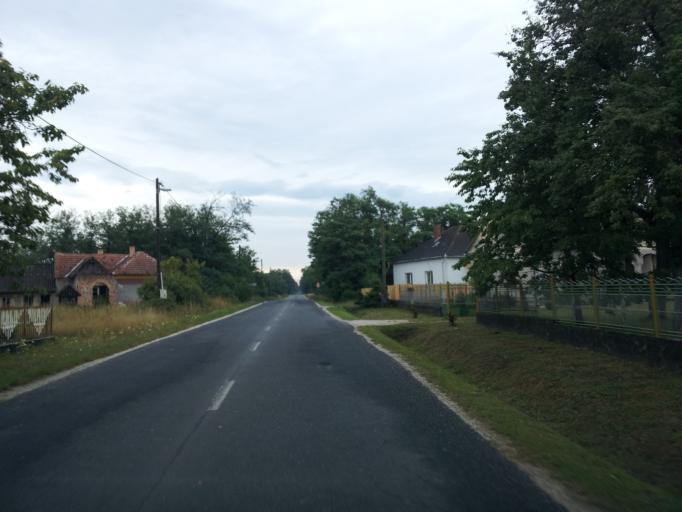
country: HU
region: Zala
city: Zalalovo
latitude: 46.8932
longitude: 16.5442
